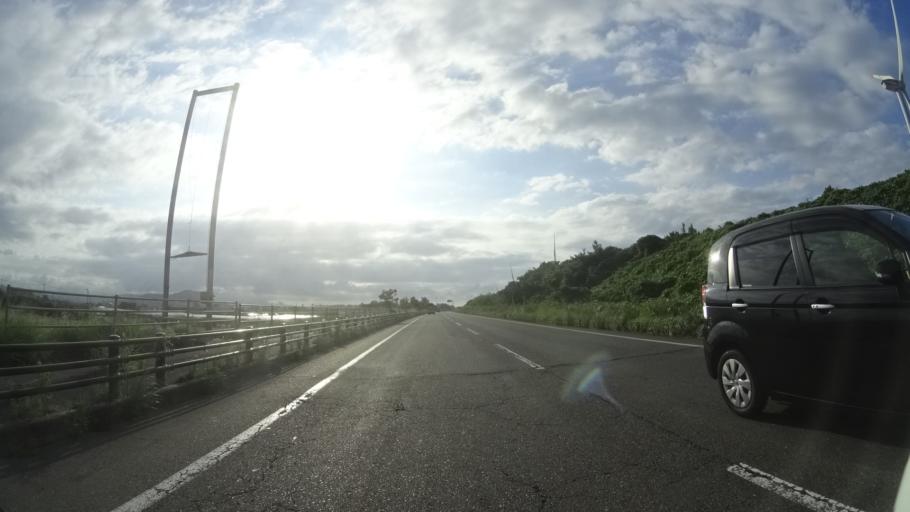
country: JP
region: Tottori
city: Kurayoshi
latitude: 35.4952
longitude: 133.8465
